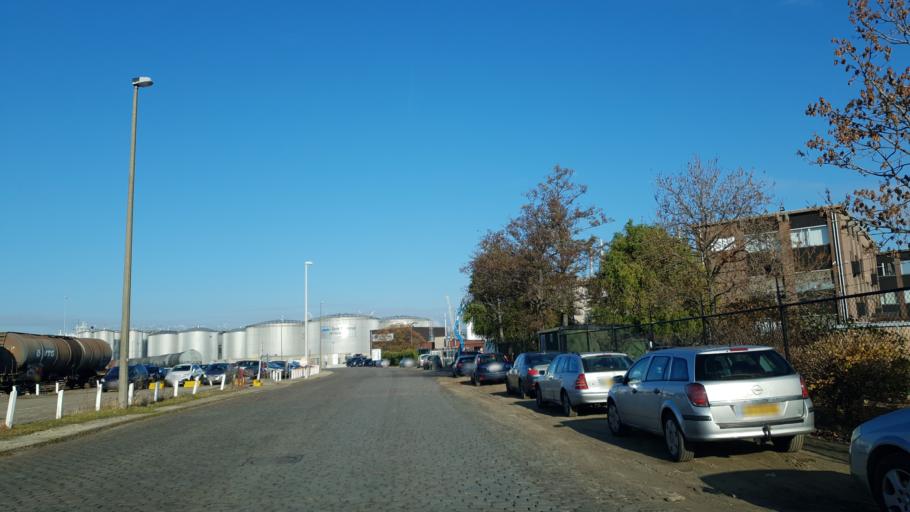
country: BE
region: Flanders
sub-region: Provincie Antwerpen
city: Zwijndrecht
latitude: 51.2587
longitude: 4.3475
